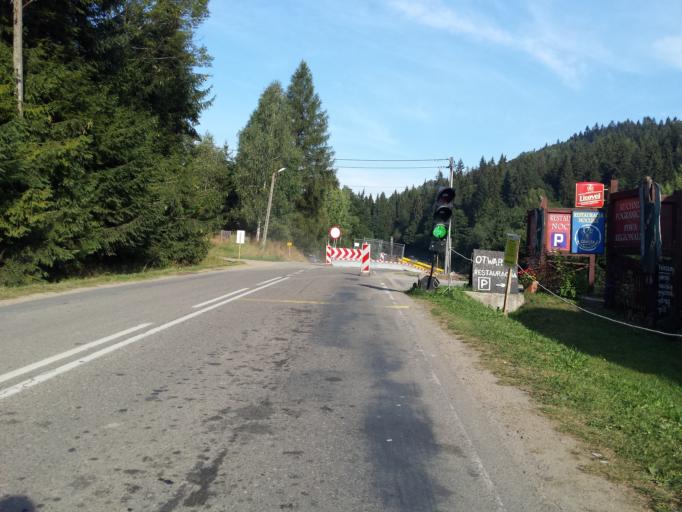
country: PL
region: Subcarpathian Voivodeship
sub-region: Powiat leski
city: Cisna
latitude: 49.2144
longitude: 22.3264
